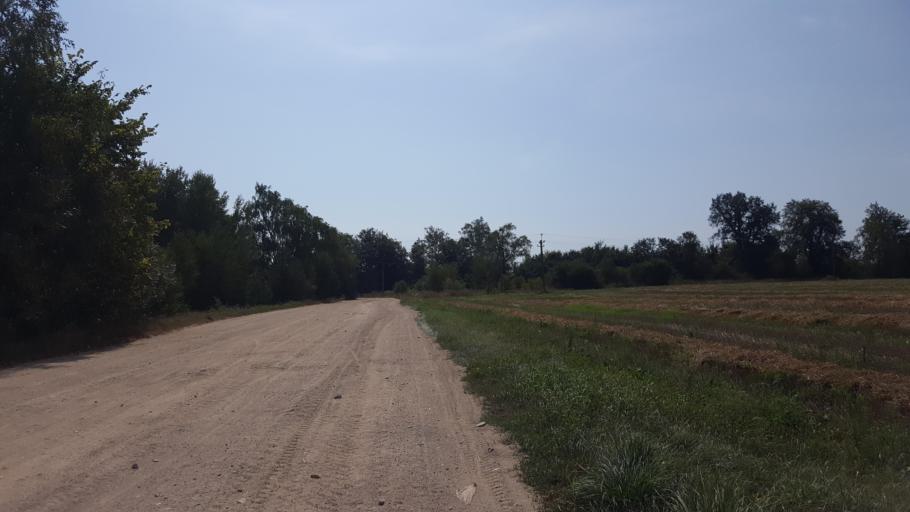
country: BY
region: Brest
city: Kamyanyuki
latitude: 52.4795
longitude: 23.7223
